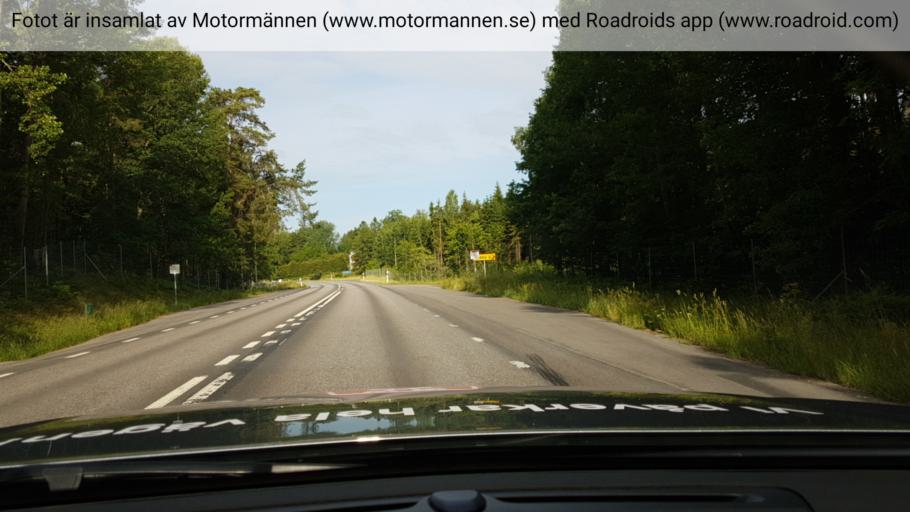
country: SE
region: OEstergoetland
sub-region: Motala Kommun
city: Borensberg
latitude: 58.5714
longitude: 15.2402
